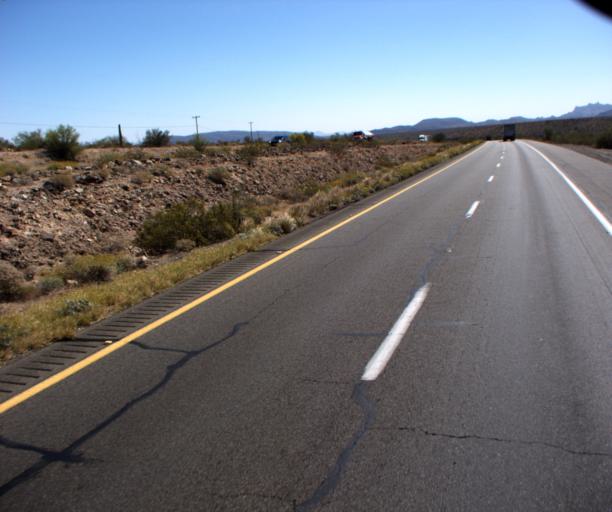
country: US
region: Arizona
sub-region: La Paz County
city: Quartzsite
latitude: 33.6661
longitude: -114.0362
